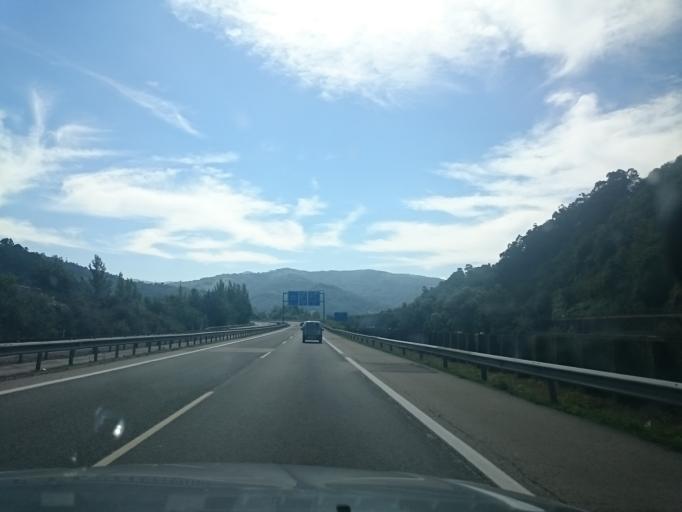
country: ES
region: Asturias
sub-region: Province of Asturias
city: Mieres
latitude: 43.2666
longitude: -5.7974
